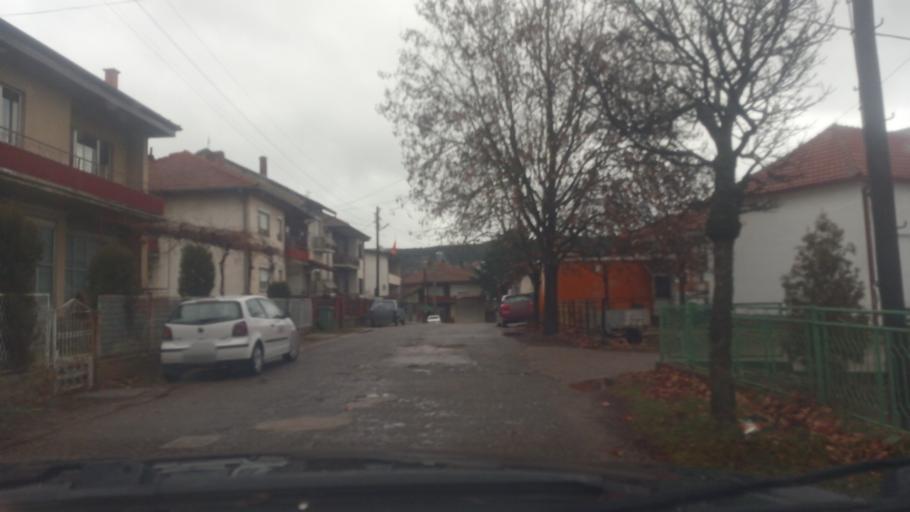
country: MK
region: Pehcevo
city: Pehcevo
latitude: 41.7627
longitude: 22.8844
